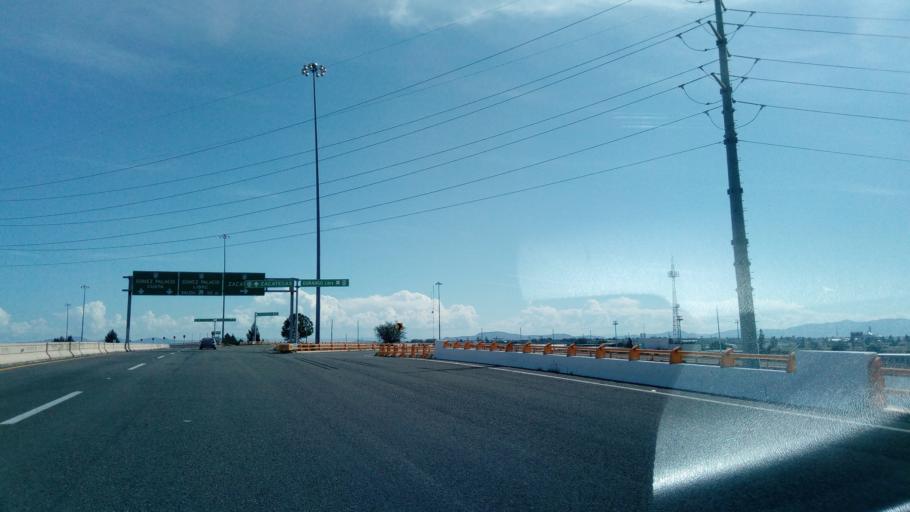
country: MX
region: Durango
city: Victoria de Durango
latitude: 24.0946
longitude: -104.5774
